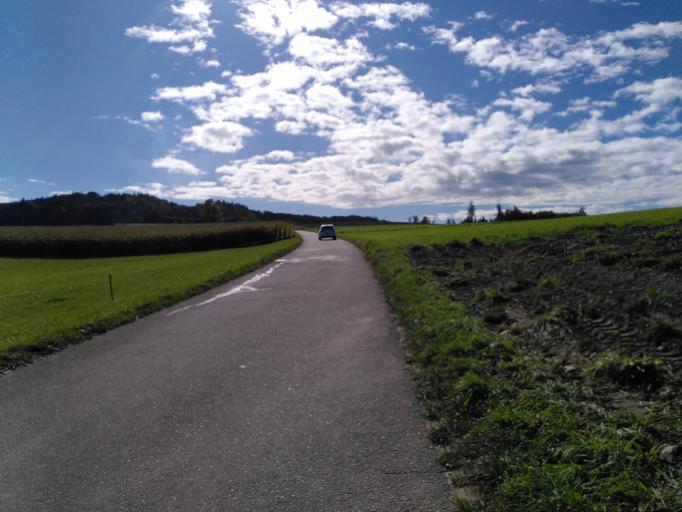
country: CH
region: Bern
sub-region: Oberaargau
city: Seeberg
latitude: 47.1379
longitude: 7.7144
